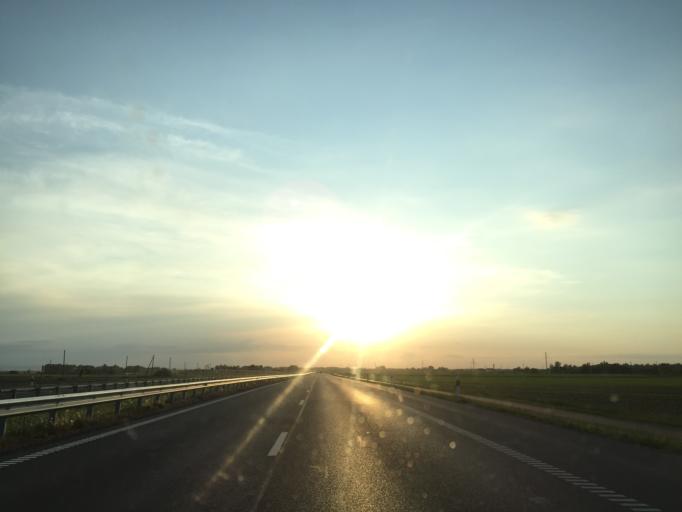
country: LT
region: Siauliu apskritis
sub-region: Siauliai
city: Siauliai
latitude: 55.9724
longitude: 23.1753
